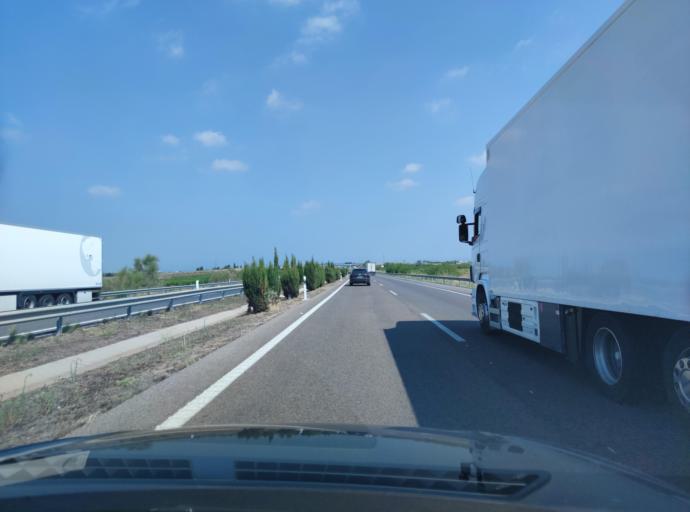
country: ES
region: Valencia
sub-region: Provincia de Castello
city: Alquerias del Nino Perdido
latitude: 39.8828
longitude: -0.1249
